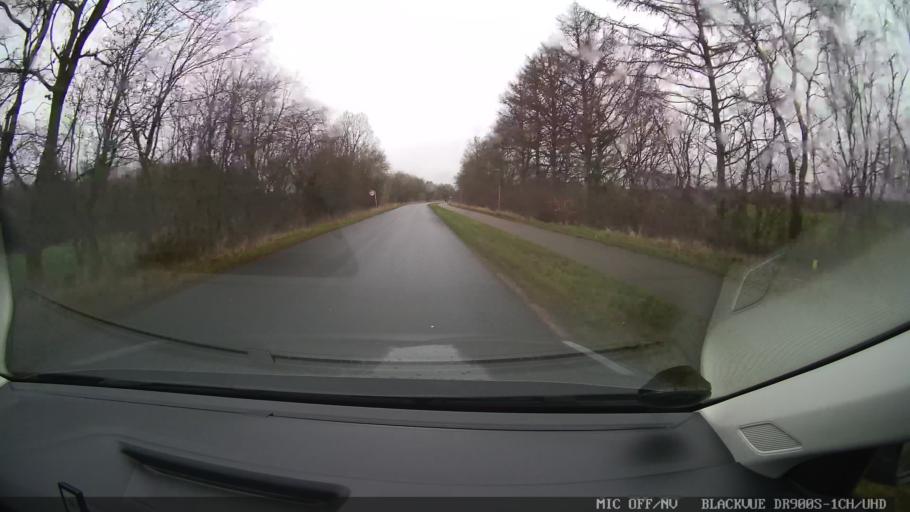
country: DK
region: Central Jutland
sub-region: Viborg Kommune
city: Karup
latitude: 56.2978
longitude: 9.1476
